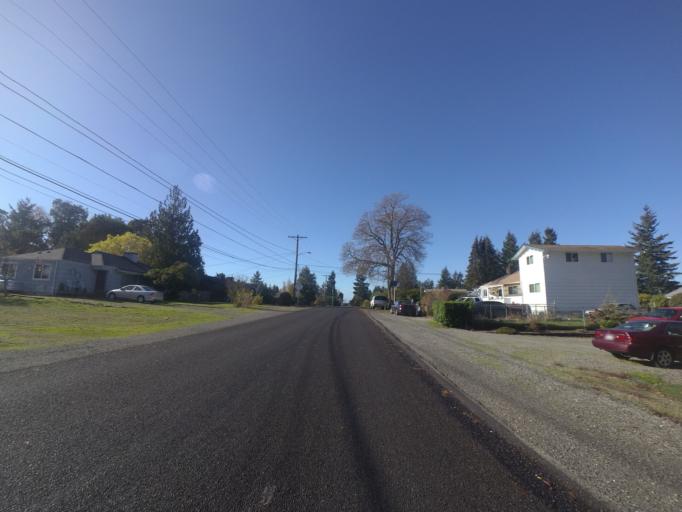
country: US
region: Washington
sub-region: Pierce County
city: University Place
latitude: 47.2280
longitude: -122.5522
